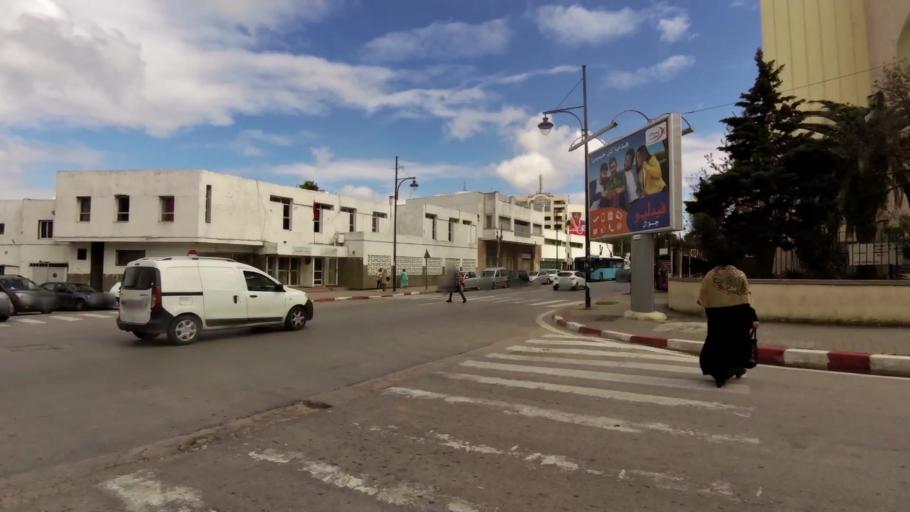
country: MA
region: Tanger-Tetouan
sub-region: Tanger-Assilah
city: Tangier
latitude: 35.7822
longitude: -5.8180
